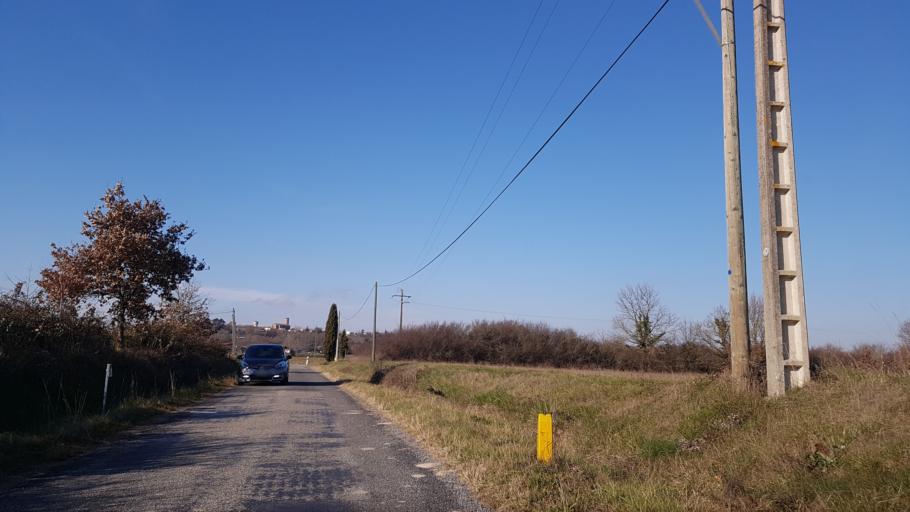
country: FR
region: Midi-Pyrenees
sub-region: Departement de l'Ariege
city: Mazeres
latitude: 43.1800
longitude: 1.6532
